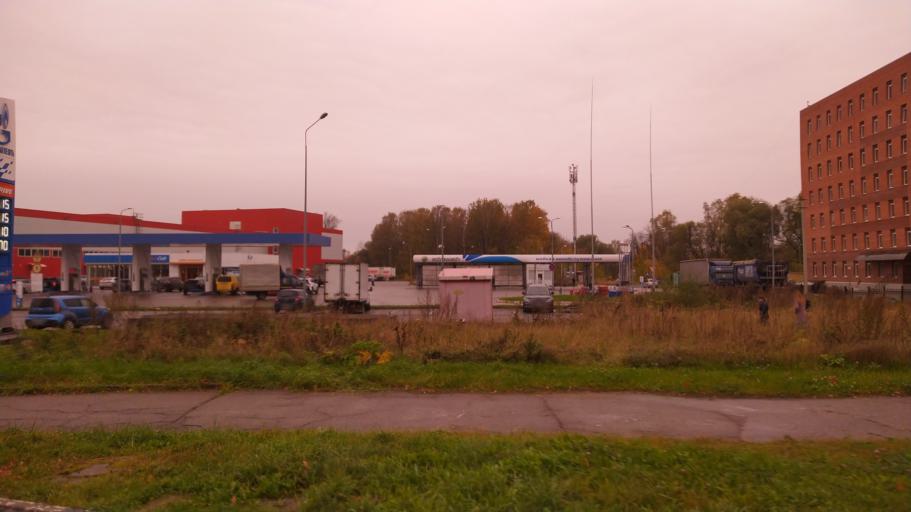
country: RU
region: Tverskaya
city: Tver
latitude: 56.8287
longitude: 35.8975
